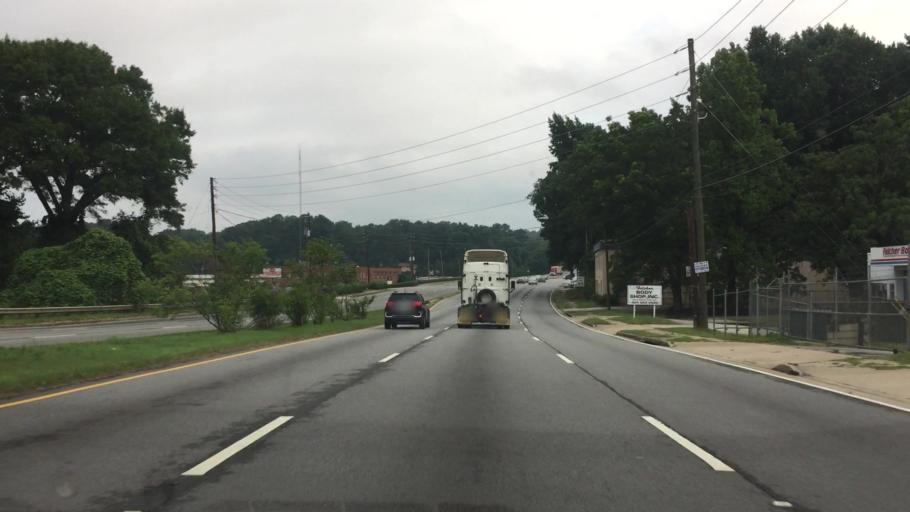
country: US
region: Georgia
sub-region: DeKalb County
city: Gresham Park
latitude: 33.6861
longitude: -84.3486
